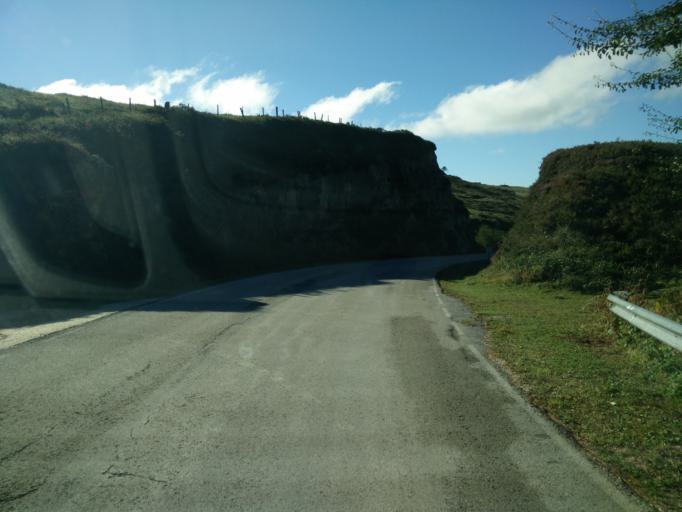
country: ES
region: Cantabria
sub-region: Provincia de Cantabria
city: San Pedro del Romeral
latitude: 43.0388
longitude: -3.8594
